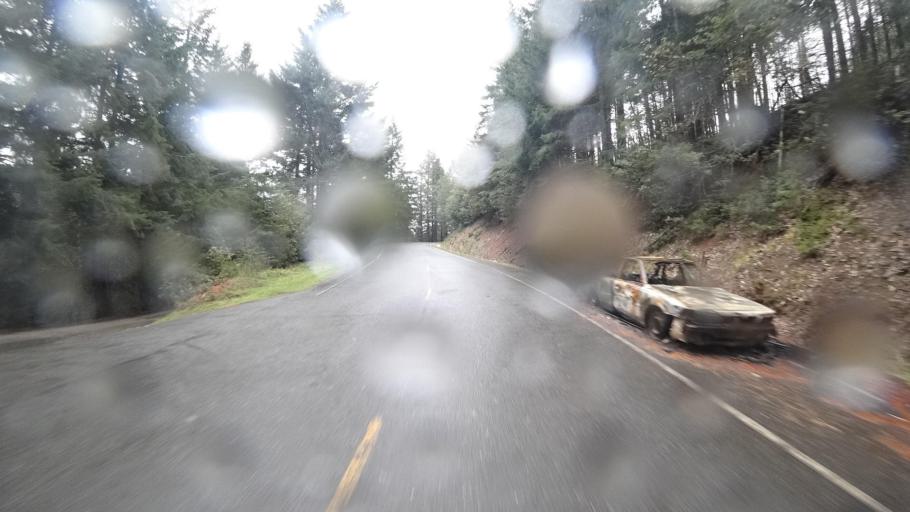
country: US
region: California
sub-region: Humboldt County
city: Willow Creek
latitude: 41.1584
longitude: -123.8180
